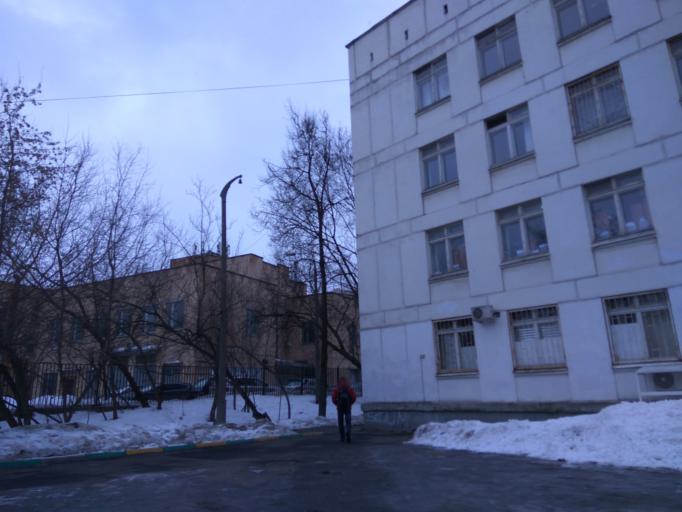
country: RU
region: Moscow
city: Biryulevo
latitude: 55.5907
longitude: 37.6689
